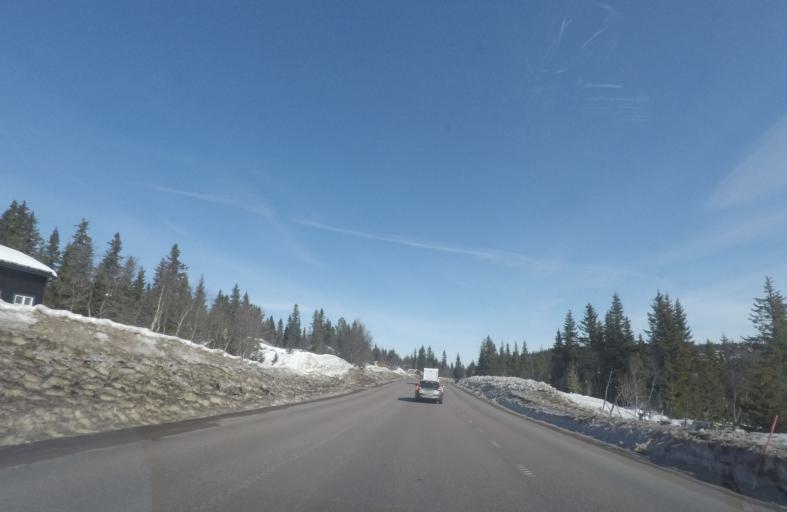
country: SE
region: Dalarna
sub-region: Malung-Saelens kommun
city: Malung
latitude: 61.1596
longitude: 13.1378
